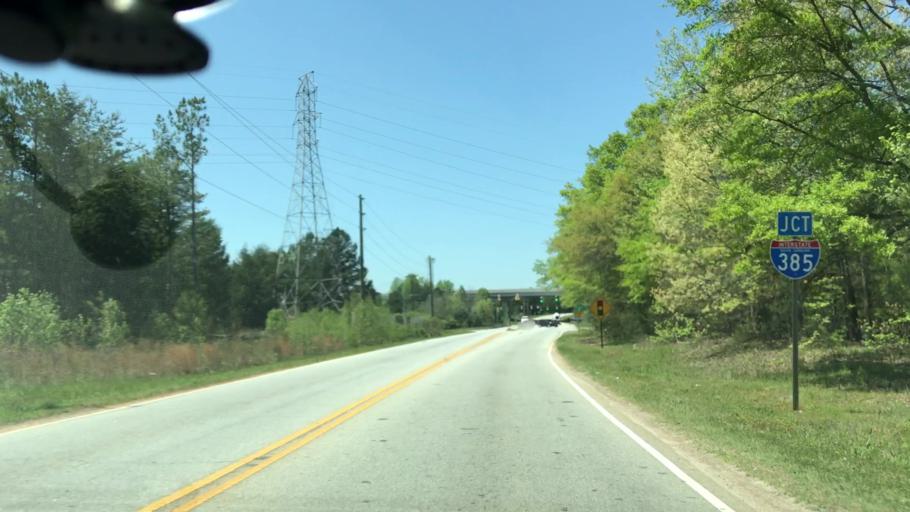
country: US
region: South Carolina
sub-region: Greenville County
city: Simpsonville
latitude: 34.7562
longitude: -82.2826
